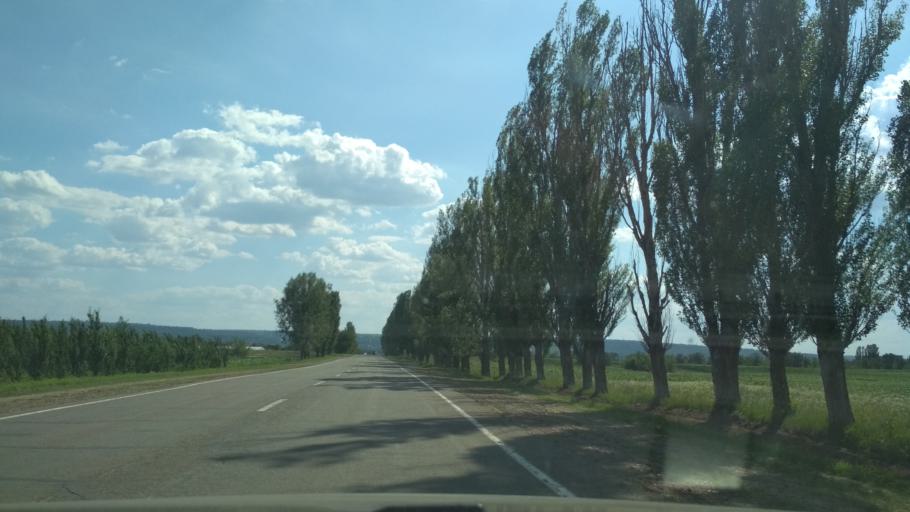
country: MD
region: Chisinau
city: Vadul lui Voda
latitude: 47.1252
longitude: 29.1184
